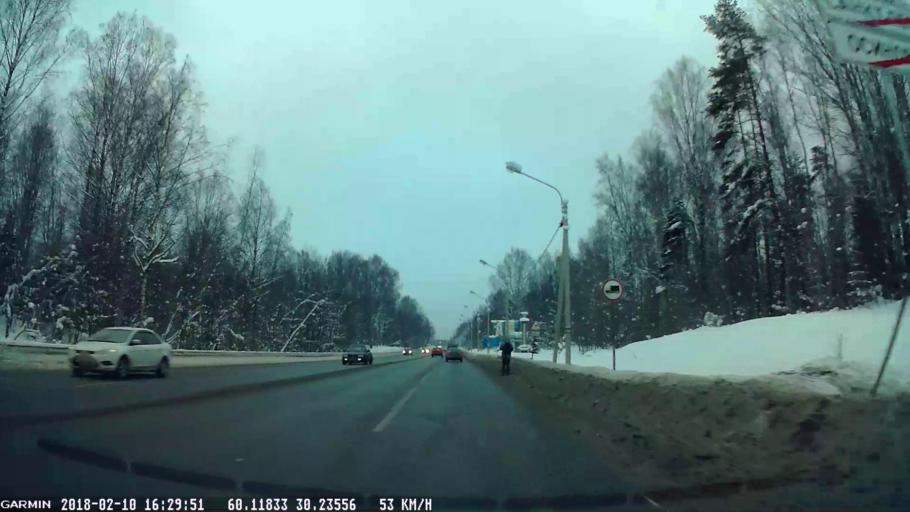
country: RU
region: St.-Petersburg
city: Levashovo
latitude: 60.1188
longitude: 30.2351
